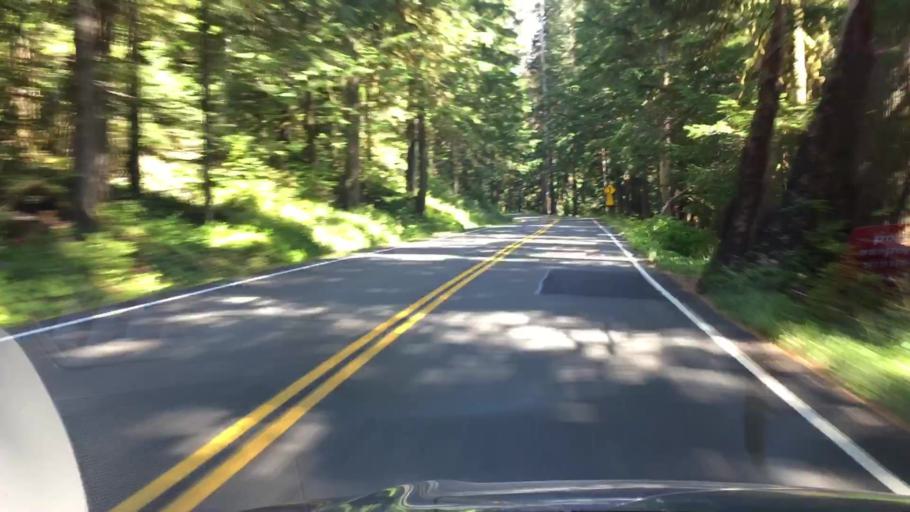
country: US
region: Washington
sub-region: Pierce County
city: Eatonville
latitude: 46.7352
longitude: -121.8497
